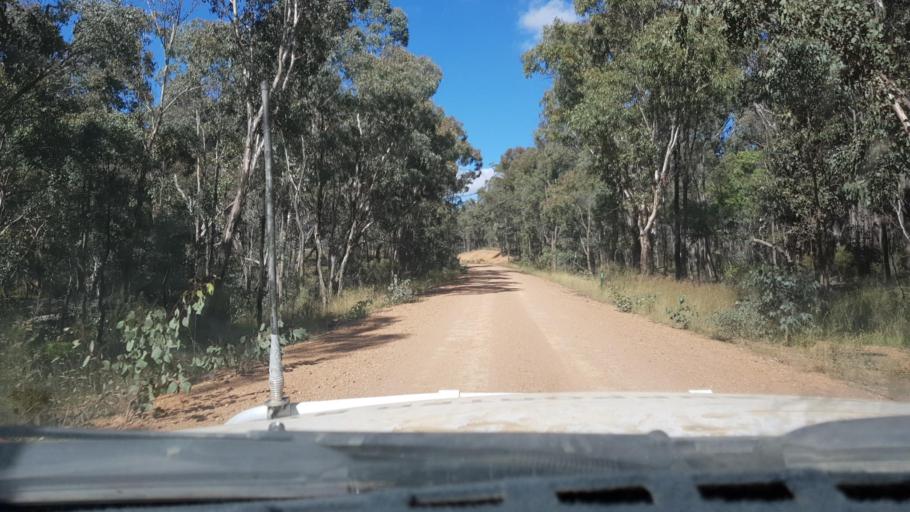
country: AU
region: New South Wales
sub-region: Tamworth Municipality
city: Manilla
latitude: -30.4523
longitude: 150.8769
